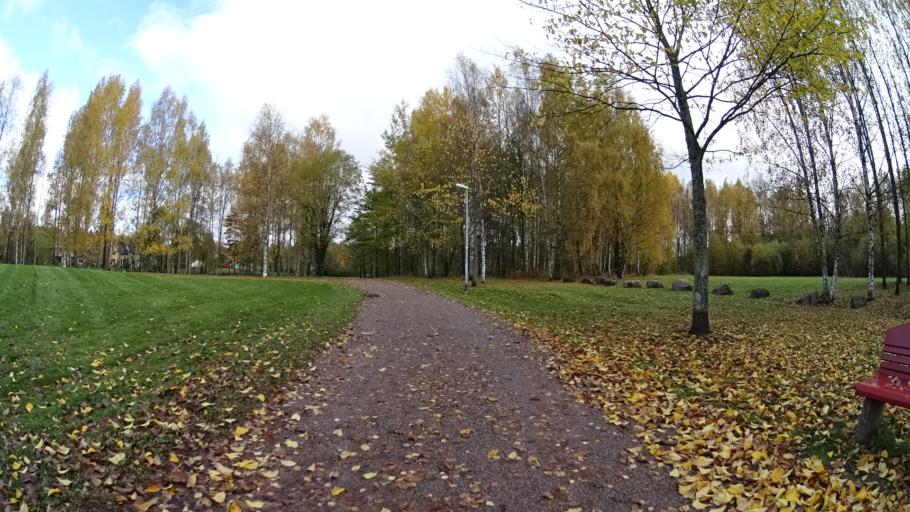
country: FI
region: Uusimaa
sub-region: Helsinki
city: Teekkarikylae
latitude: 60.2738
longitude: 24.8629
